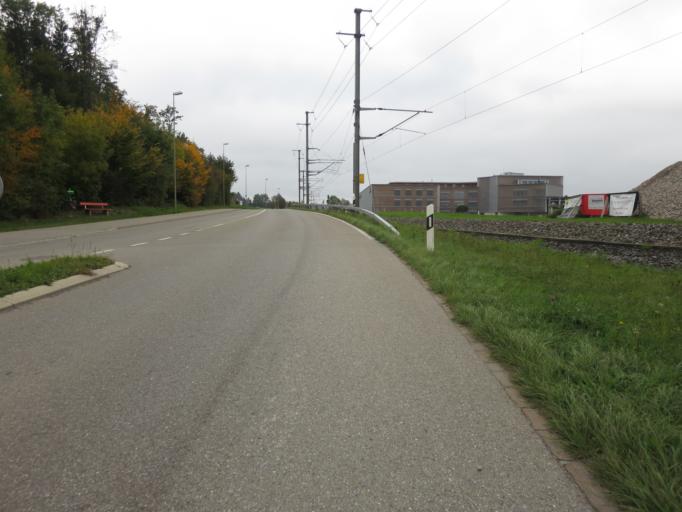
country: CH
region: Zurich
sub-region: Bezirk Hinwil
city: Bubikon
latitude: 47.2743
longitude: 8.8184
